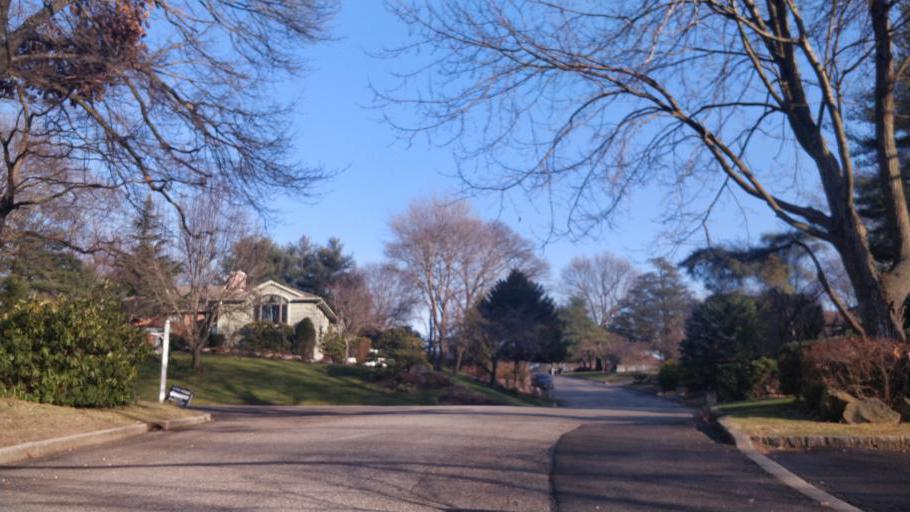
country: US
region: New York
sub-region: Nassau County
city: Bayville
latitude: 40.9023
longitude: -73.5678
